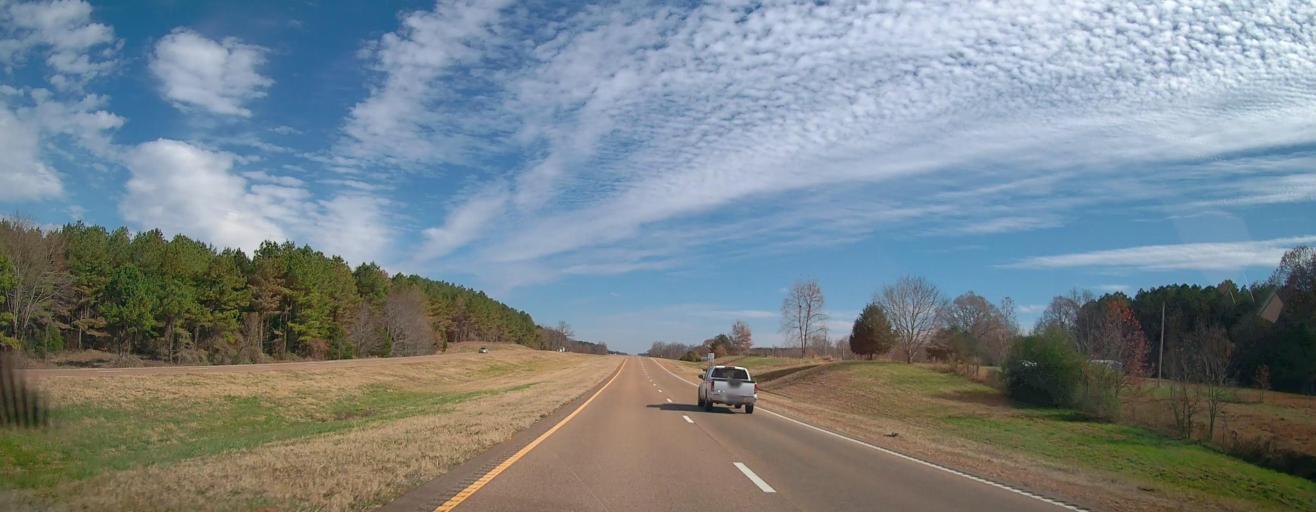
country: US
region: Mississippi
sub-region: Benton County
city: Ashland
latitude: 34.9477
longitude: -89.1153
